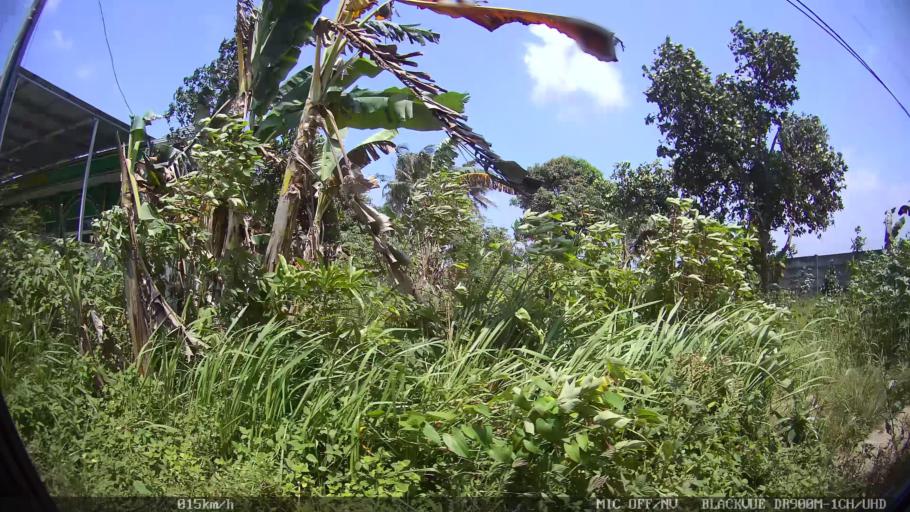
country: ID
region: Lampung
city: Kedaton
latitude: -5.3516
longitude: 105.2789
